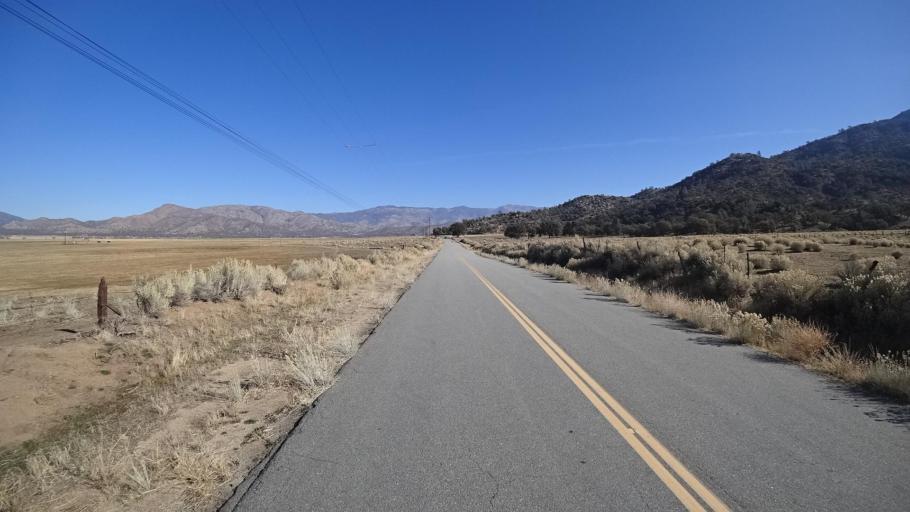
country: US
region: California
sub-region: Kern County
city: Bodfish
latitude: 35.3903
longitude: -118.5318
